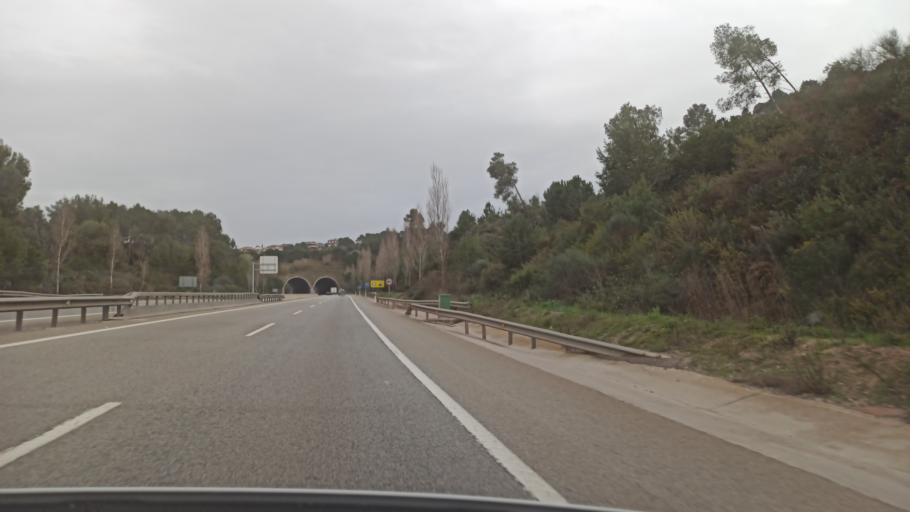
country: ES
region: Catalonia
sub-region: Provincia de Barcelona
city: Cervello
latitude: 41.3918
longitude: 1.9574
